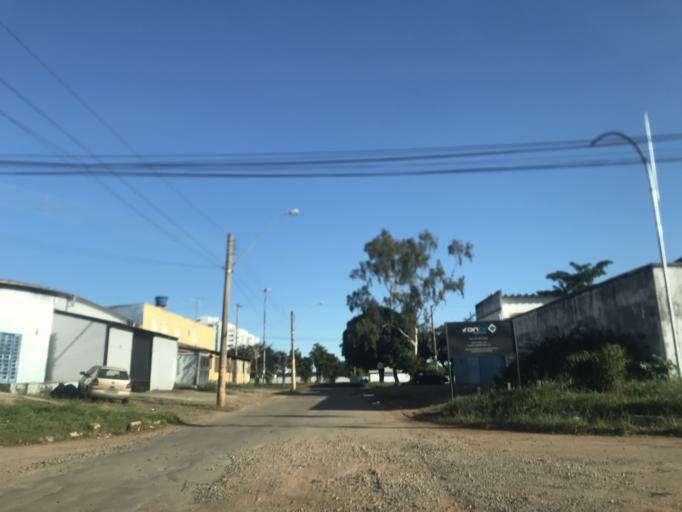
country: BR
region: Federal District
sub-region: Brasilia
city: Brasilia
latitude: -15.8263
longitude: -47.9587
